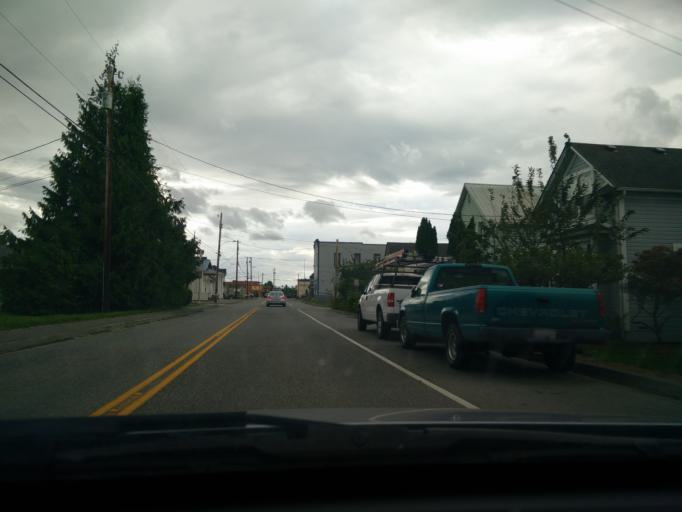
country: US
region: Washington
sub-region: Snohomish County
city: Stanwood
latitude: 48.2441
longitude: -122.3707
